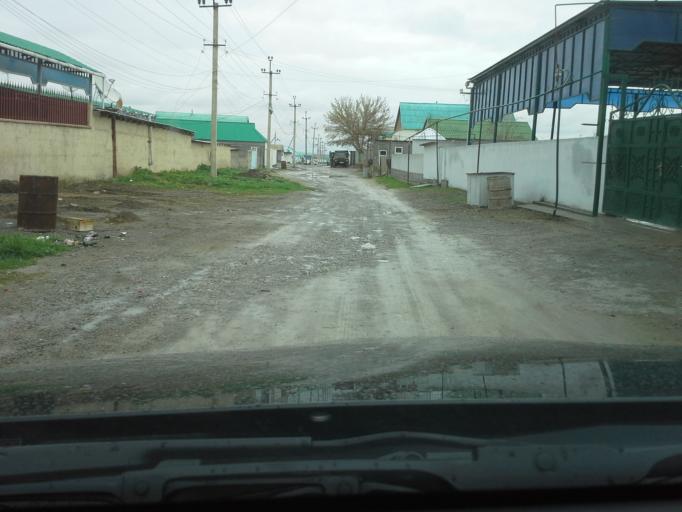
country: TM
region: Ahal
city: Abadan
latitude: 37.9644
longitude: 58.2086
